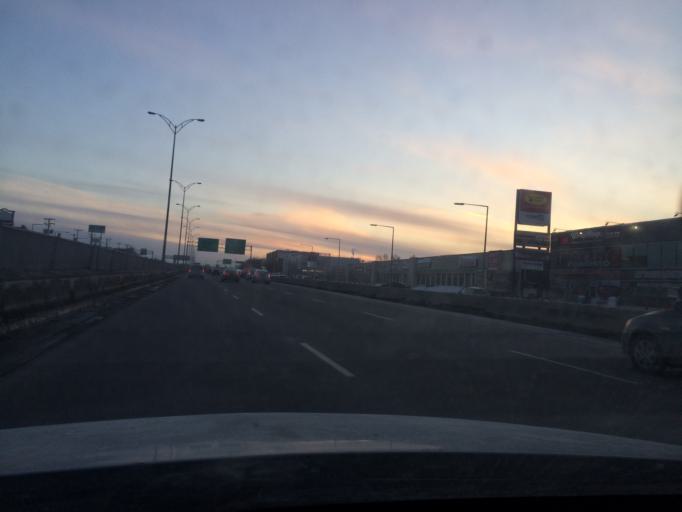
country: CA
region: Quebec
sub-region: Montreal
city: Saint-Leonard
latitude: 45.5874
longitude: -73.5844
